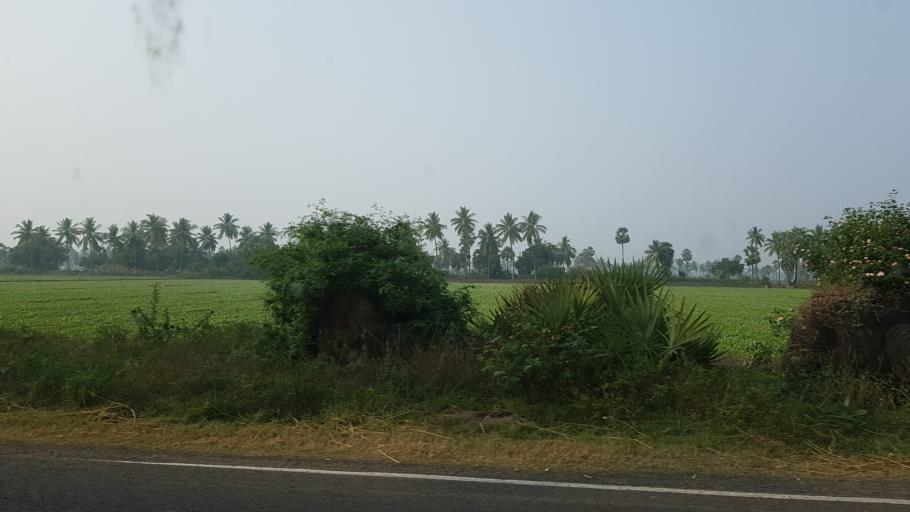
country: IN
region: Andhra Pradesh
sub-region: Krishna
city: Korukollu
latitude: 16.4907
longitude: 81.2532
